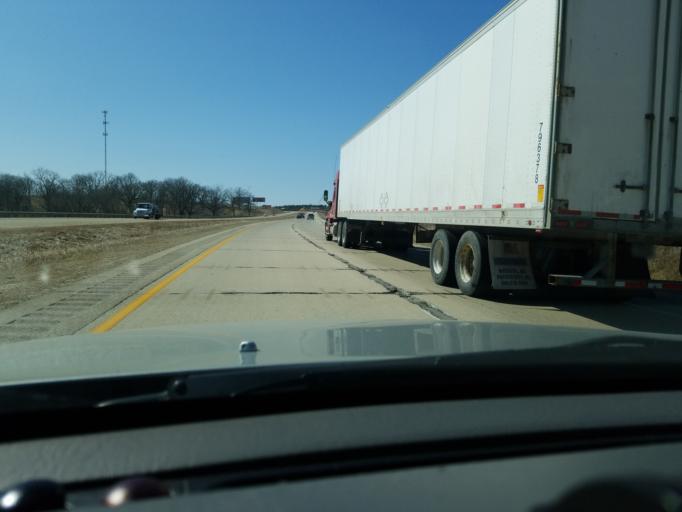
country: US
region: Wisconsin
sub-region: Iowa County
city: Barneveld
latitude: 42.9959
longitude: -89.9881
